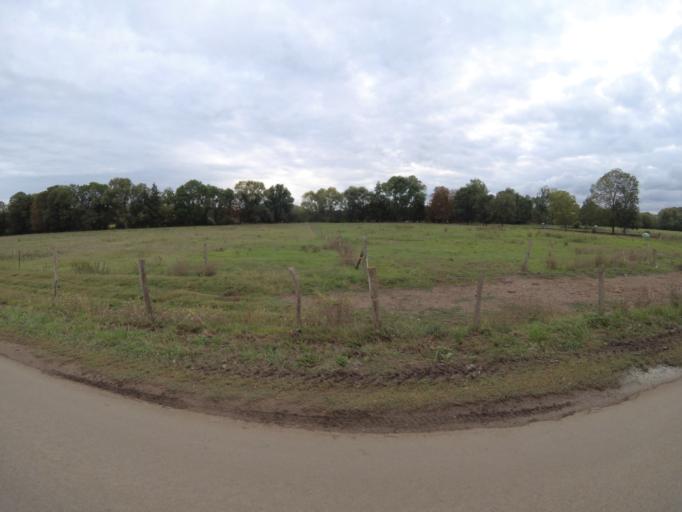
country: FR
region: Ile-de-France
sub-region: Departement de Seine-et-Marne
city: Gouvernes
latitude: 48.8604
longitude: 2.6806
